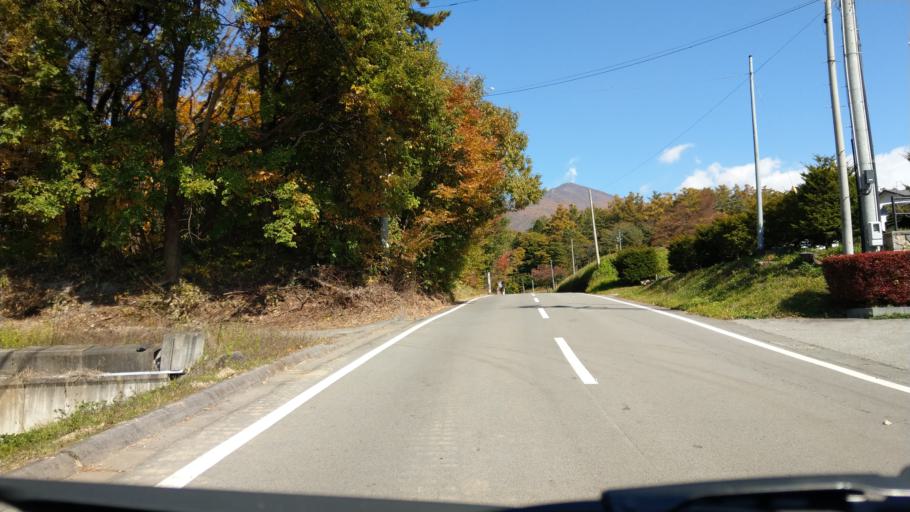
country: JP
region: Nagano
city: Komoro
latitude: 36.3544
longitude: 138.4496
